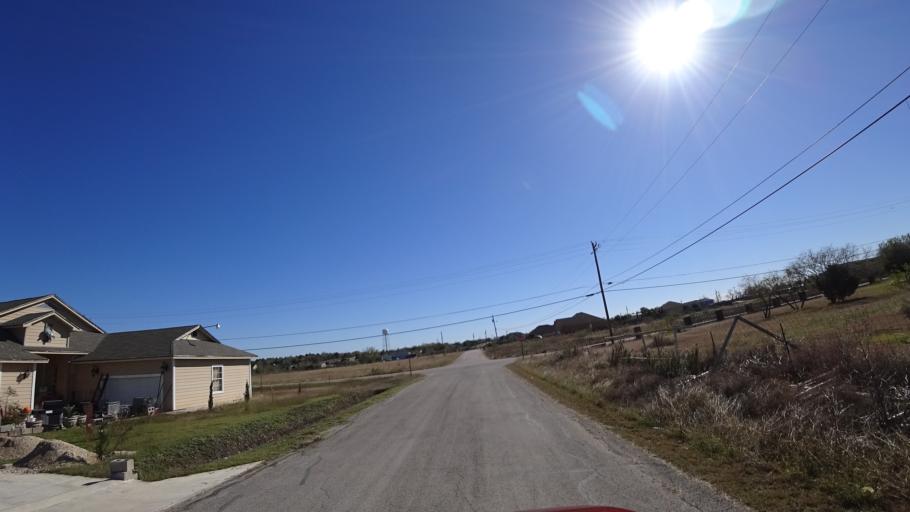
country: US
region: Texas
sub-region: Travis County
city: Garfield
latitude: 30.1025
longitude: -97.6056
